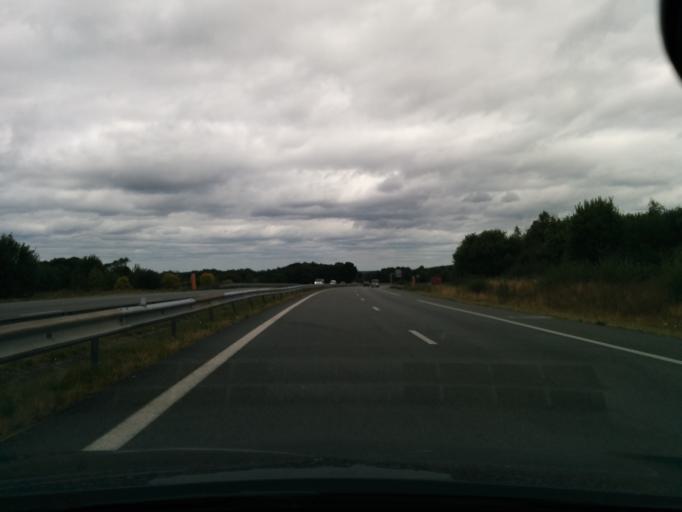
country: FR
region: Limousin
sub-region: Departement de la Creuse
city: Saint-Maurice-la-Souterraine
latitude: 46.2051
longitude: 1.3824
